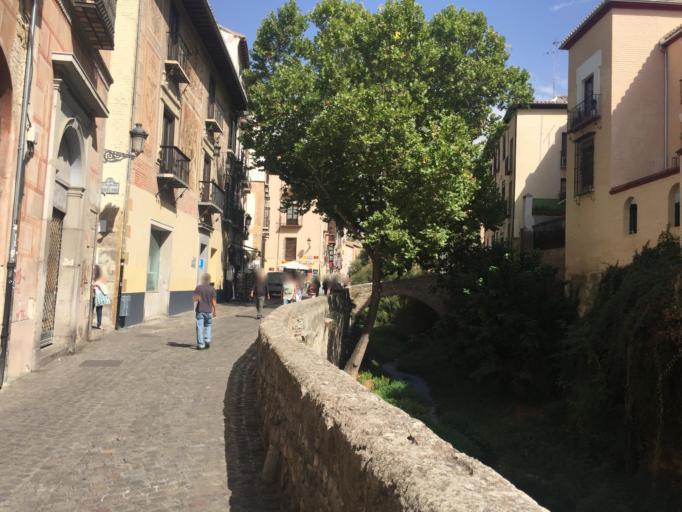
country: ES
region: Andalusia
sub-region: Provincia de Granada
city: Granada
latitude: 37.1778
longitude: -3.5942
